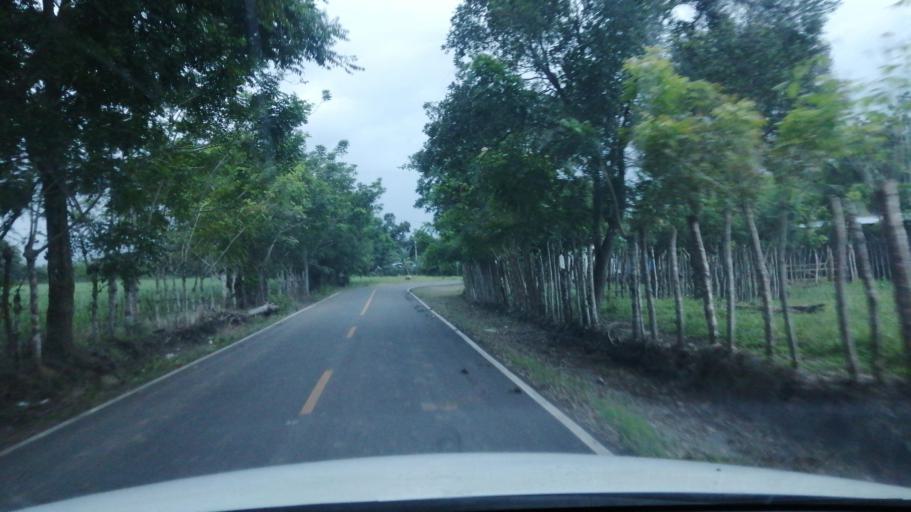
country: PA
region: Chiriqui
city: Alanje
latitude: 8.4197
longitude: -82.5047
